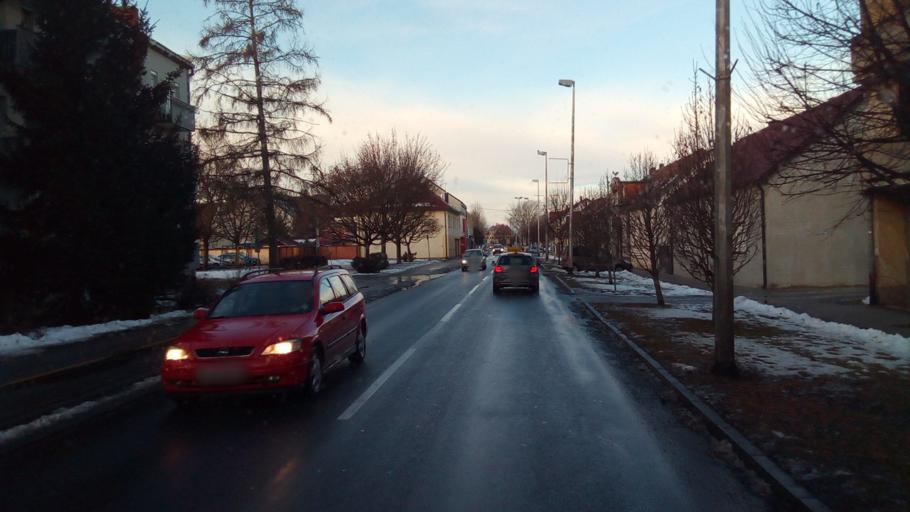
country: HR
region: Medimurska
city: Cakovec
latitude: 46.3911
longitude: 16.4387
